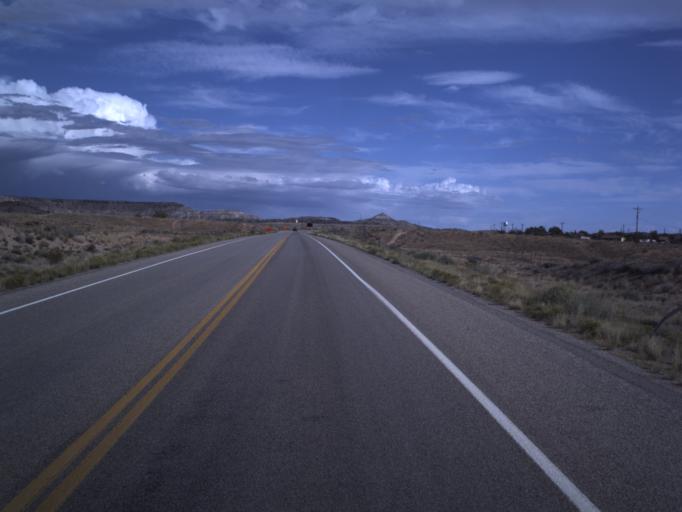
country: US
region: Colorado
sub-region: Montezuma County
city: Towaoc
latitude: 37.2099
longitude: -109.1709
